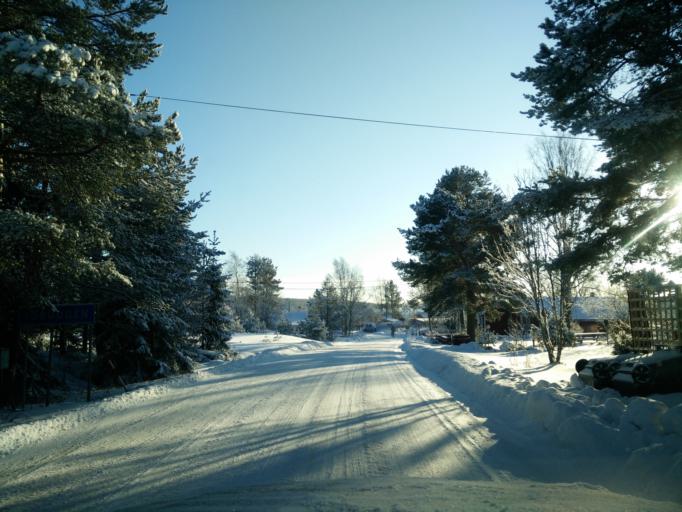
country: SE
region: Vaesternorrland
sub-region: Sundsvalls Kommun
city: Njurundabommen
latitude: 62.2328
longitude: 17.6547
